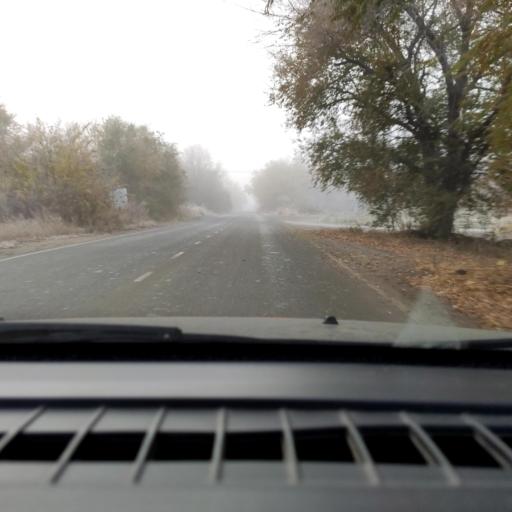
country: RU
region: Samara
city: Tol'yatti
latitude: 53.5837
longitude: 49.2568
